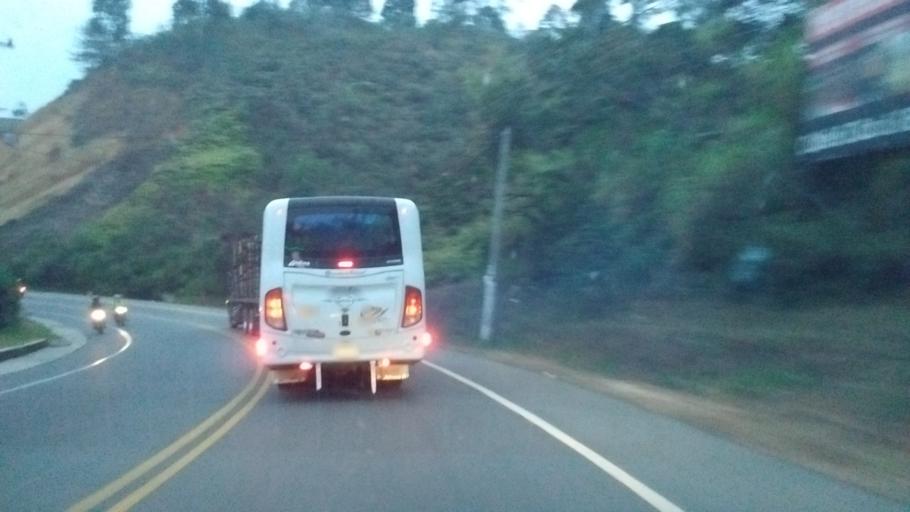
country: CO
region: Cauca
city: Popayan
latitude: 2.4235
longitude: -76.6286
